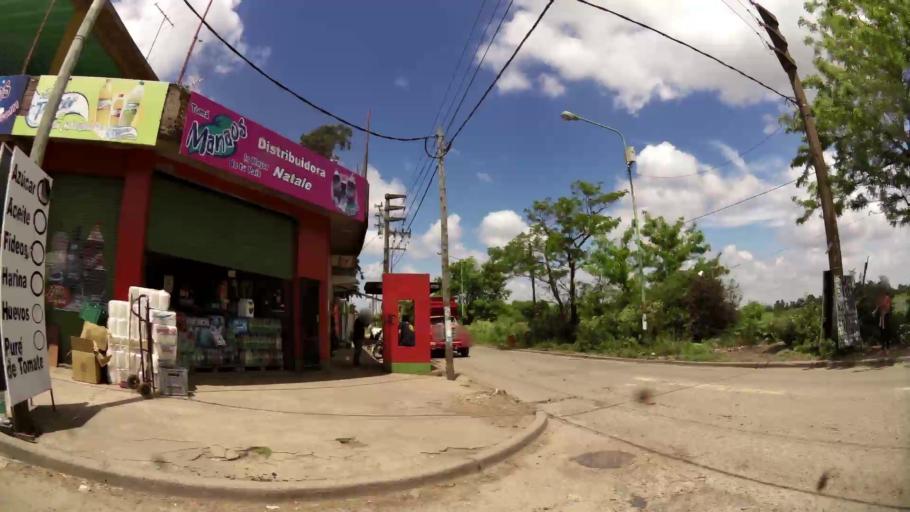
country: AR
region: Buenos Aires
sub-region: Partido de Quilmes
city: Quilmes
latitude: -34.8256
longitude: -58.2466
